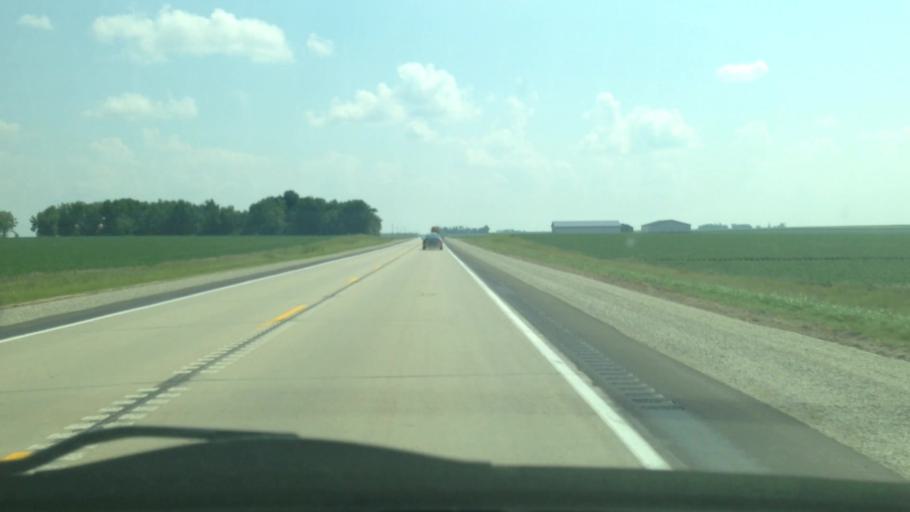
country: US
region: Iowa
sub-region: Howard County
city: Cresco
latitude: 43.4258
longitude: -92.2986
